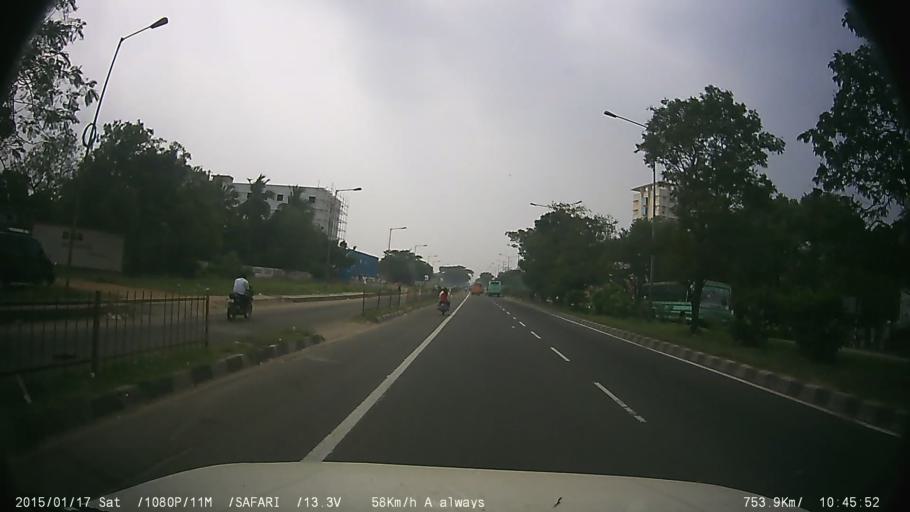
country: IN
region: Tamil Nadu
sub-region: Kancheepuram
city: Vandalur
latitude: 12.8749
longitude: 80.0785
